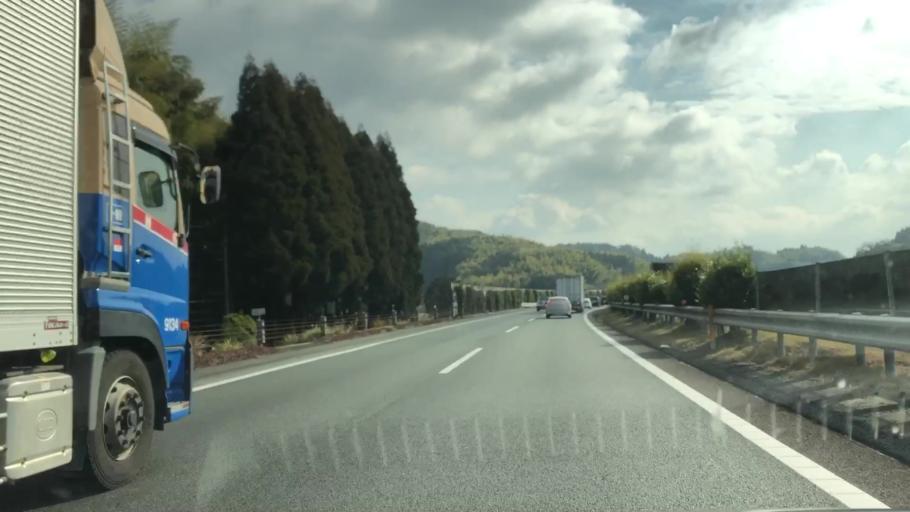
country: JP
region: Fukuoka
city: Setakamachi-takayanagi
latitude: 33.0868
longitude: 130.5407
